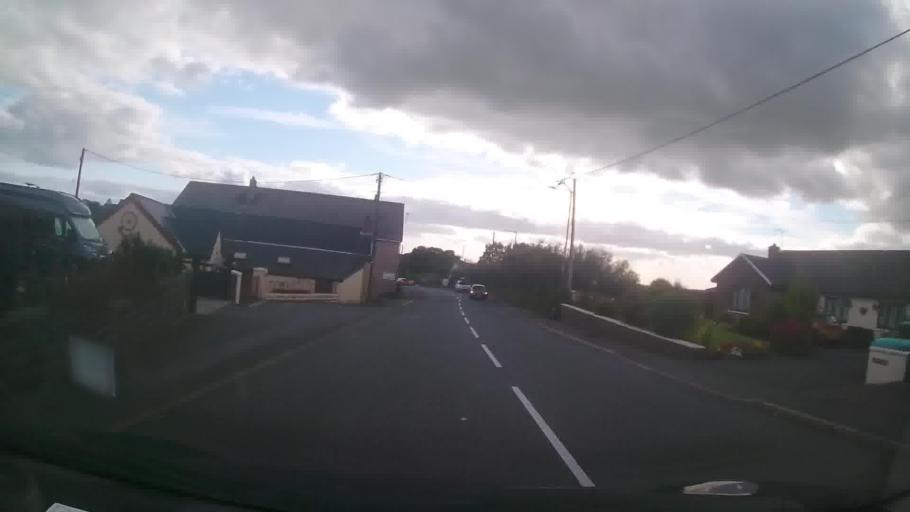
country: GB
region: Wales
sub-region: Pembrokeshire
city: Kilgetty
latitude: 51.7188
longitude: -4.7307
